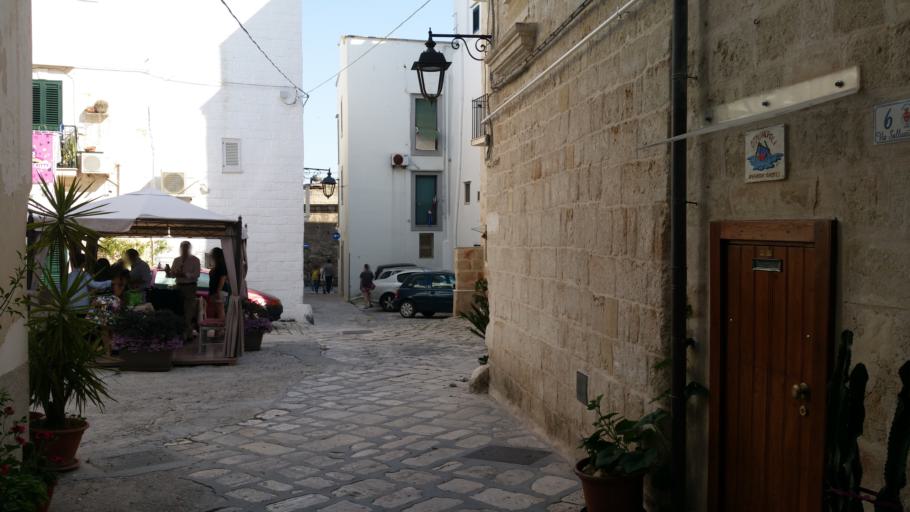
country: IT
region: Apulia
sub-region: Provincia di Bari
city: Monopoli
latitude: 40.9516
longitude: 17.3053
